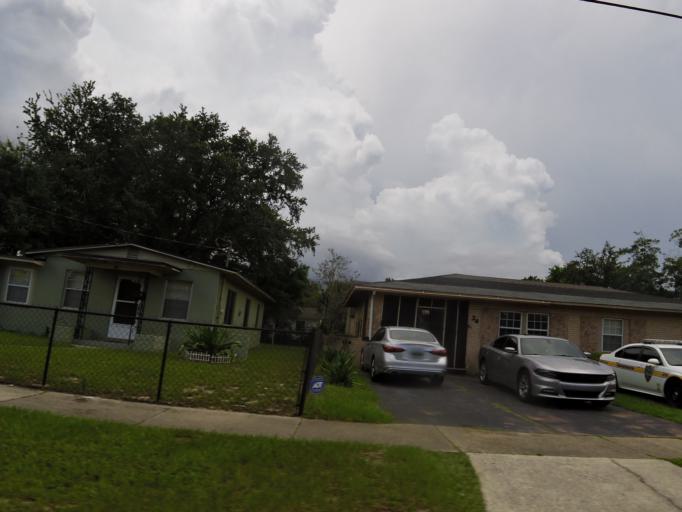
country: US
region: Florida
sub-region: Duval County
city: Jacksonville
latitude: 30.3726
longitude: -81.6525
